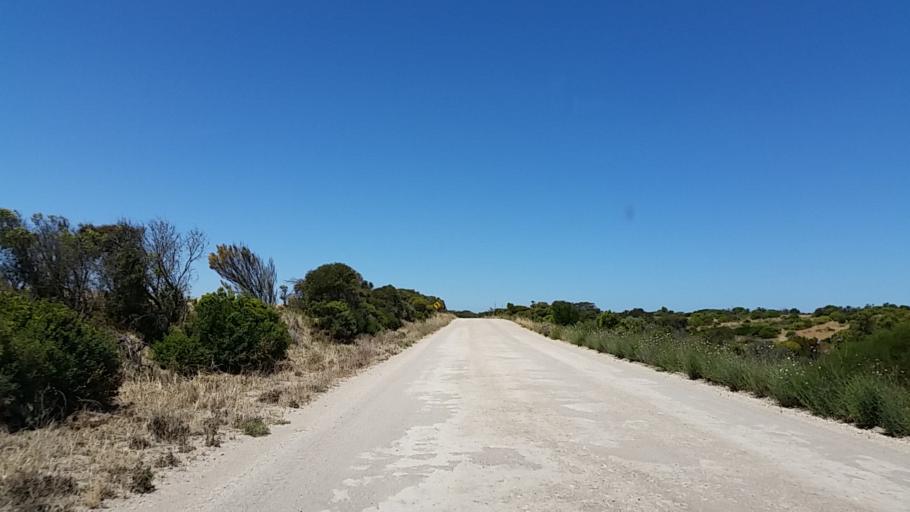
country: AU
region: South Australia
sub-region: Yorke Peninsula
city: Honiton
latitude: -35.1174
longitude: 137.3676
